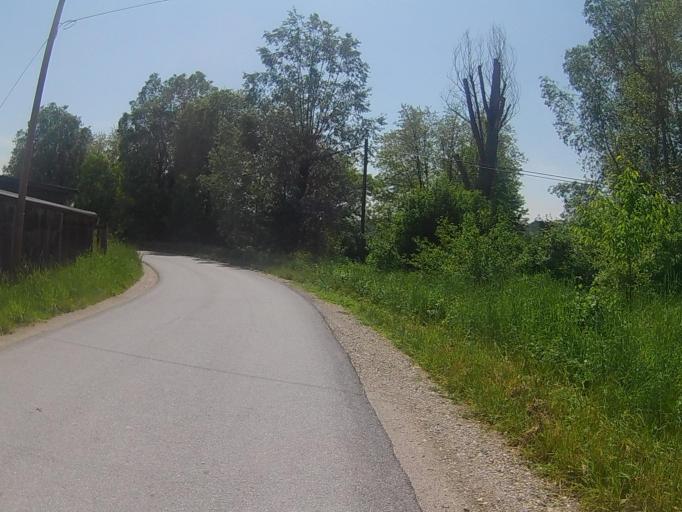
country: SI
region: Pesnica
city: Pesnica pri Mariboru
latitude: 46.5802
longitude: 15.7298
